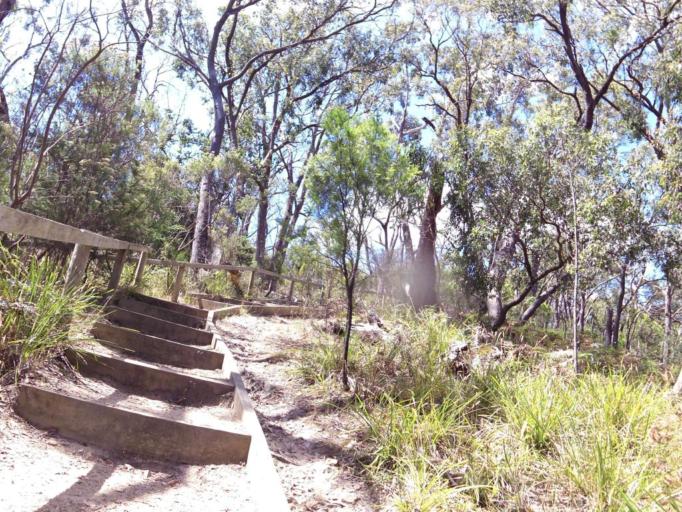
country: AU
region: Victoria
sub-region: Mornington Peninsula
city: Moorooduc
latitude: -38.2044
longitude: 145.1099
